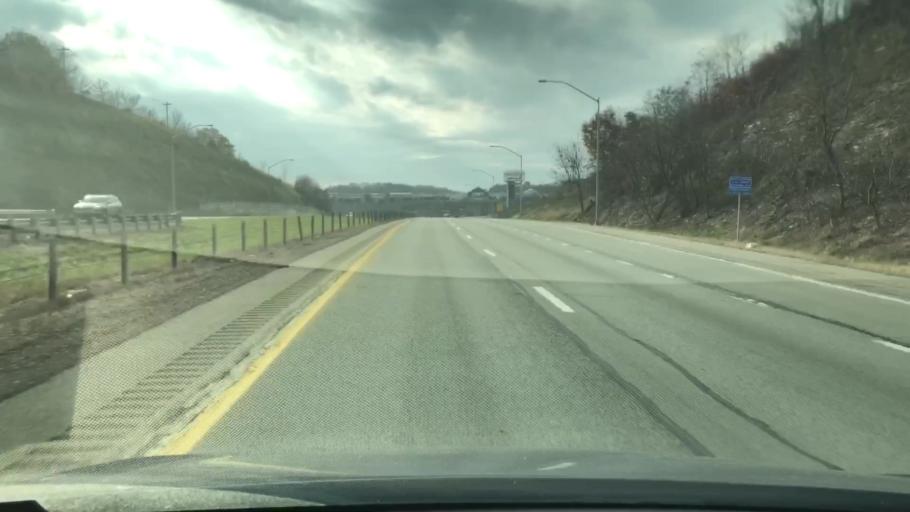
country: US
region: Pennsylvania
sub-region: Westmoreland County
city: Arnold
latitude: 40.5713
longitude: -79.7912
